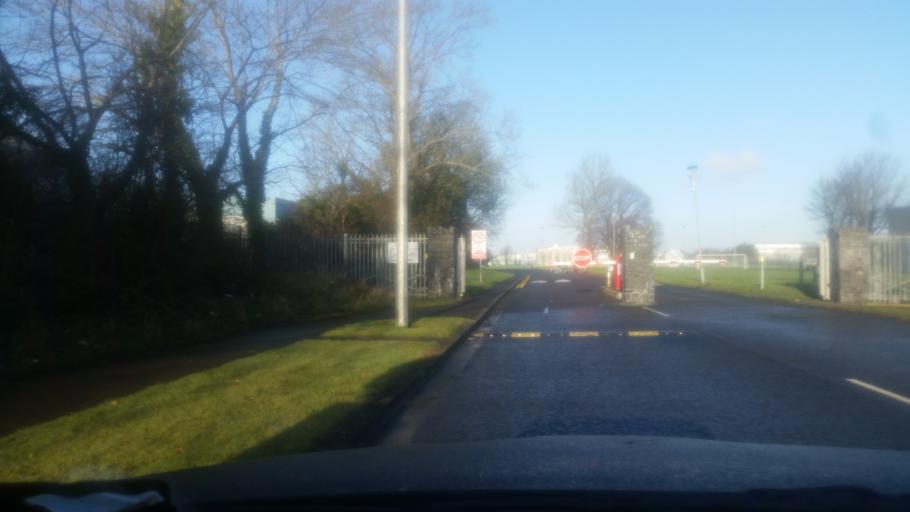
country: IE
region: Leinster
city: Beaumont
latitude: 53.4080
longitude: -6.2409
